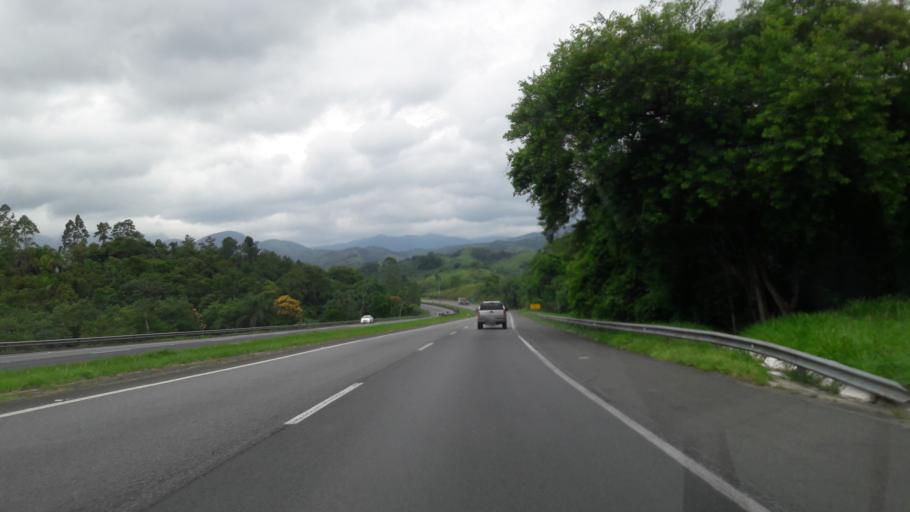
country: BR
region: Sao Paulo
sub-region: Cajati
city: Cajati
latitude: -24.7665
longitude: -48.1665
